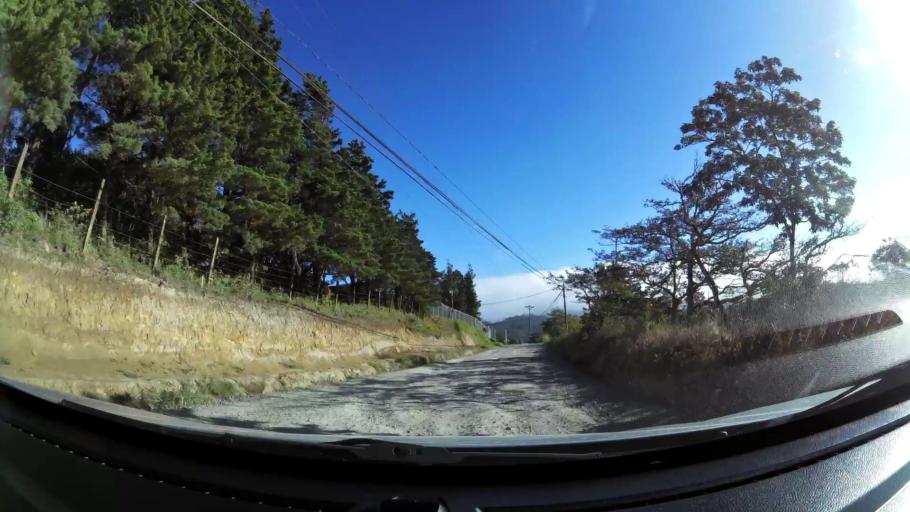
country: CR
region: Guanacaste
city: Juntas
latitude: 10.3114
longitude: -84.8287
